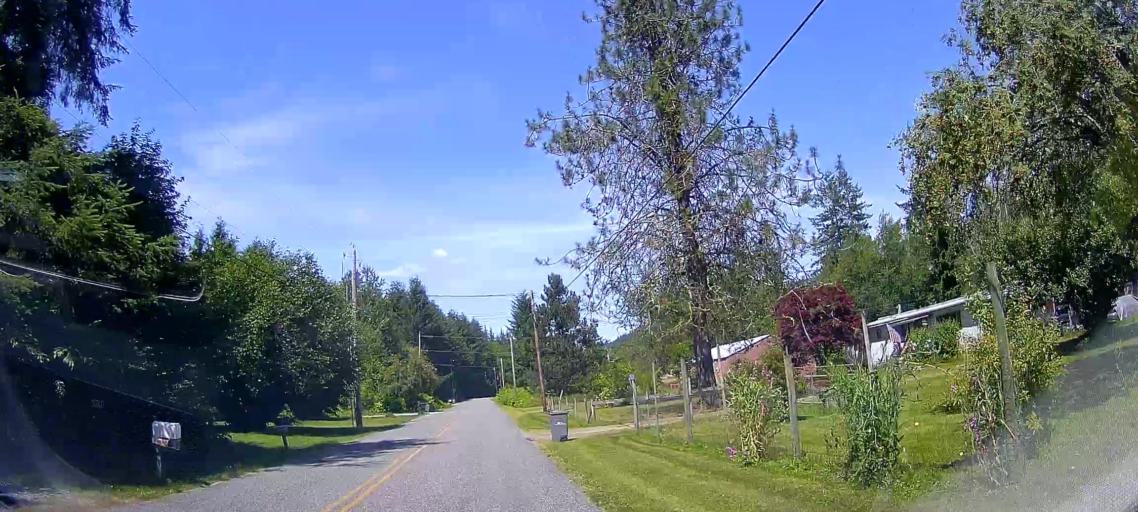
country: US
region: Washington
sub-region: Skagit County
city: Burlington
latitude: 48.5945
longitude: -122.3170
